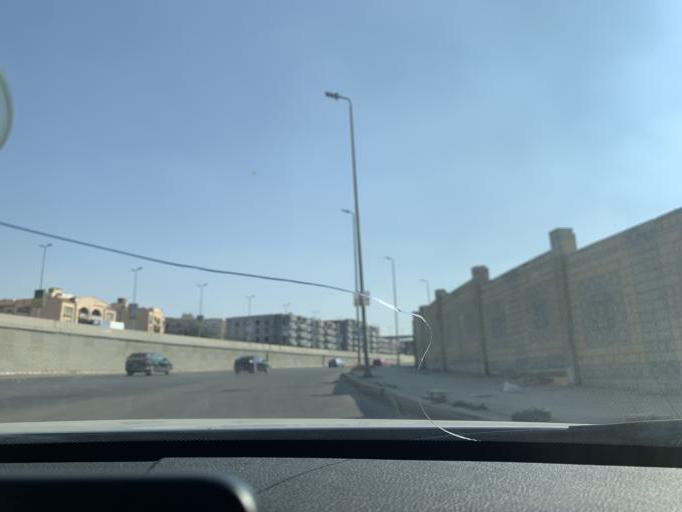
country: EG
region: Muhafazat al Qalyubiyah
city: Al Khankah
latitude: 30.0248
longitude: 31.4742
